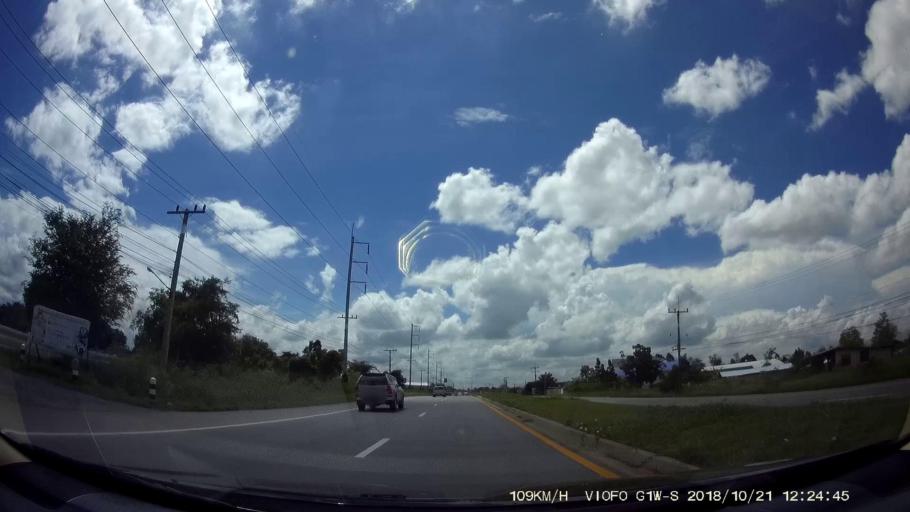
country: TH
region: Nakhon Ratchasima
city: Dan Khun Thot
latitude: 15.2296
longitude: 101.7795
